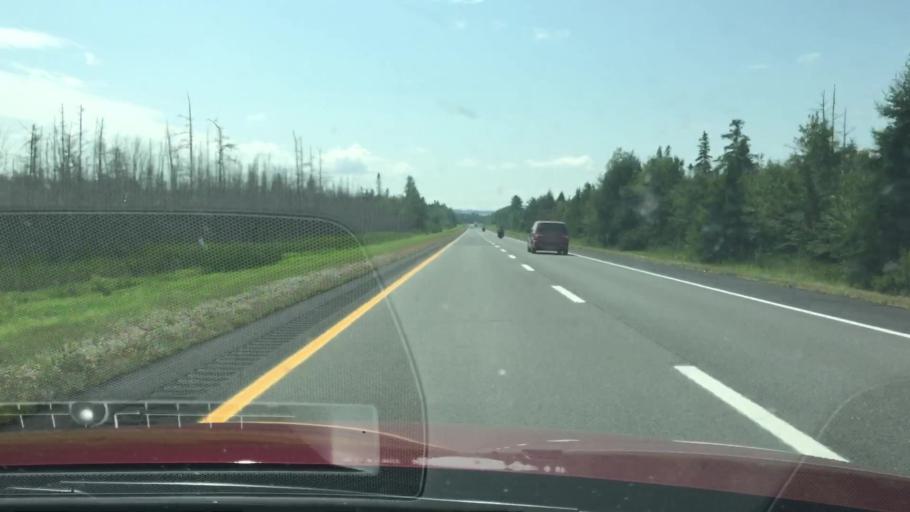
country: US
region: Maine
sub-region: Penobscot County
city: Patten
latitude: 45.9859
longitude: -68.2853
